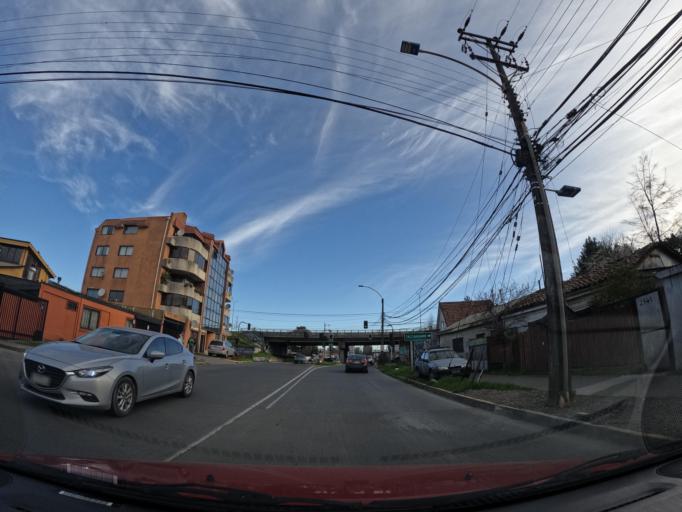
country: CL
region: Biobio
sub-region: Provincia de Concepcion
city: Concepcion
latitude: -36.8073
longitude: -73.0324
